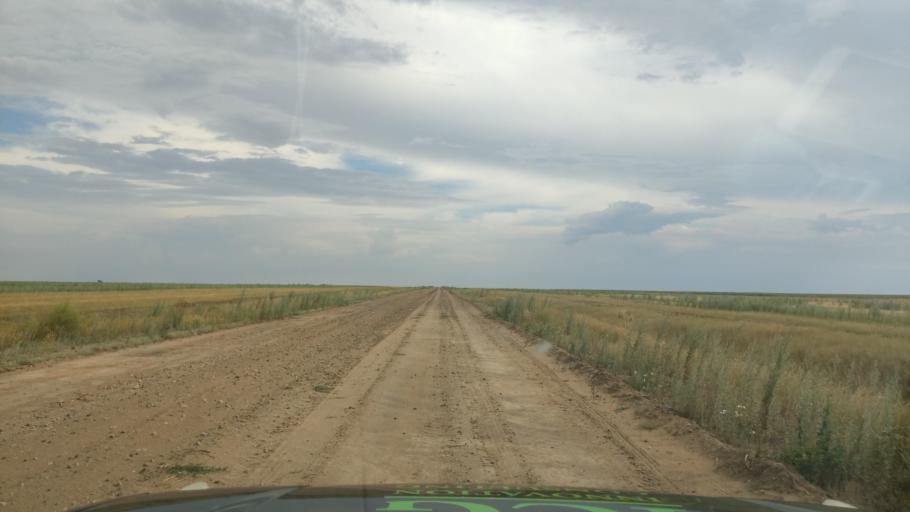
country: KZ
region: Pavlodar
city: Pavlodar
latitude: 52.5370
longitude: 77.5705
